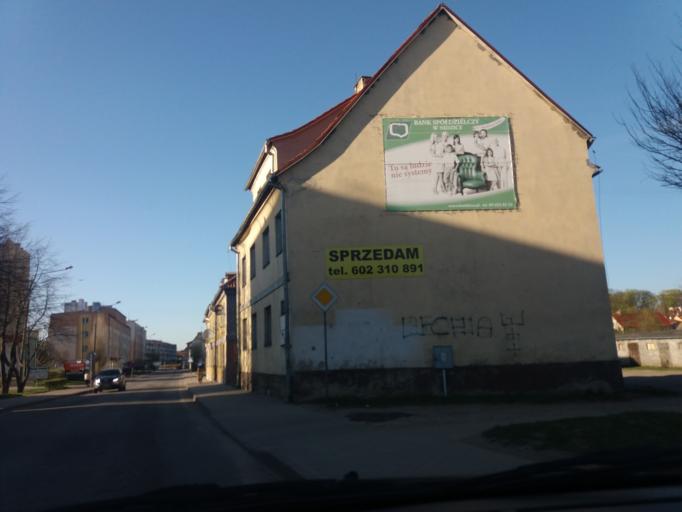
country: PL
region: Warmian-Masurian Voivodeship
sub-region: Powiat nidzicki
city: Nidzica
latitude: 53.3560
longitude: 20.4262
